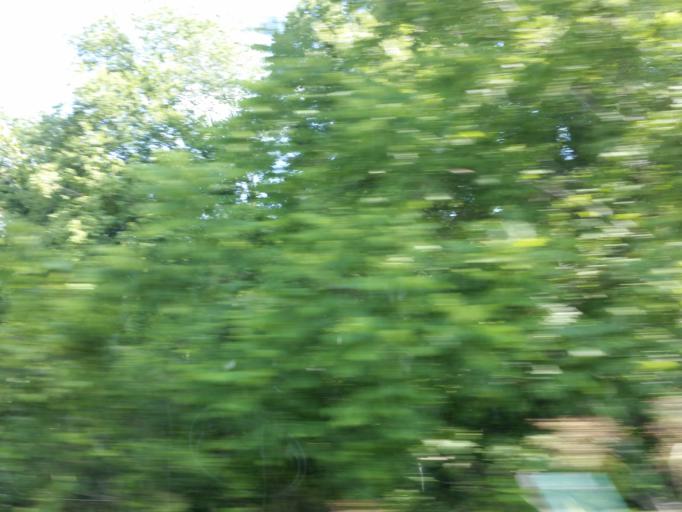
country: US
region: Tennessee
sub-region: Perry County
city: Linden
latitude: 35.6342
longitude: -87.7782
